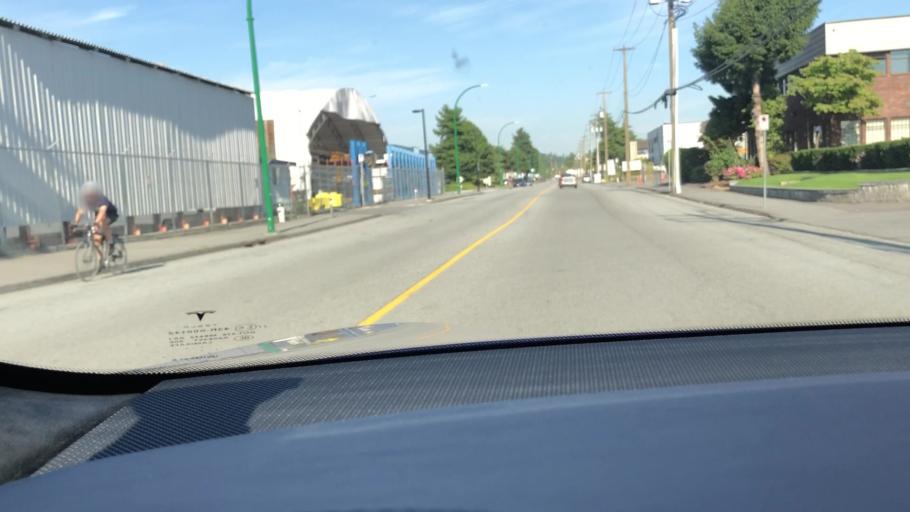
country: CA
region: British Columbia
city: Burnaby
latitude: 49.2608
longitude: -122.9923
